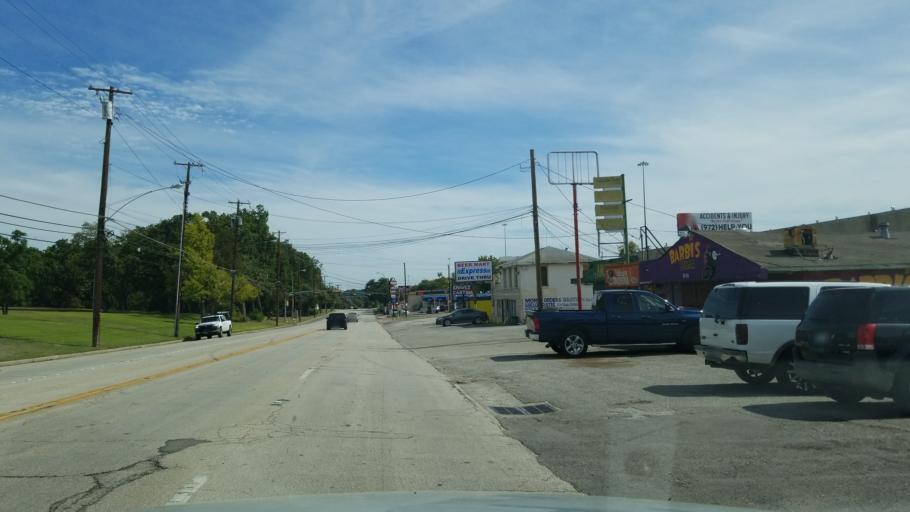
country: US
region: Texas
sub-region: Dallas County
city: Highland Park
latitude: 32.7929
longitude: -96.7392
